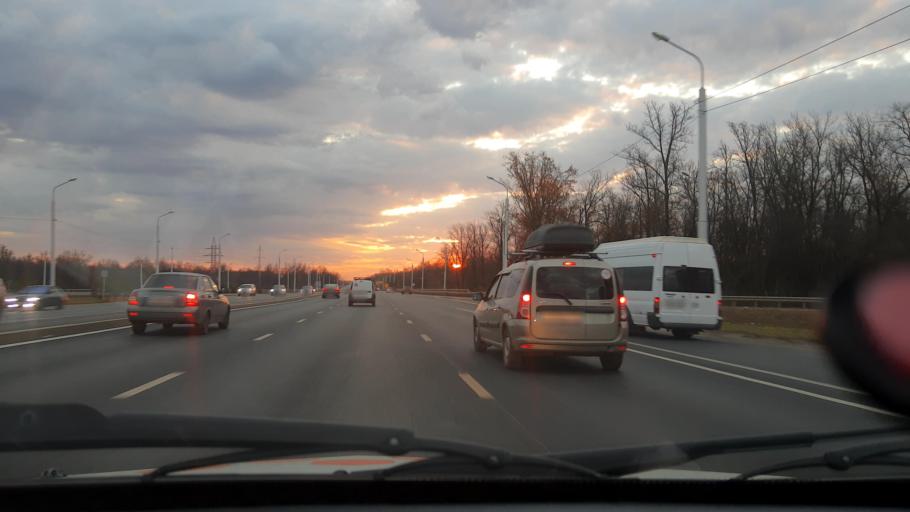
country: RU
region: Bashkortostan
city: Mikhaylovka
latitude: 54.7006
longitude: 55.8664
